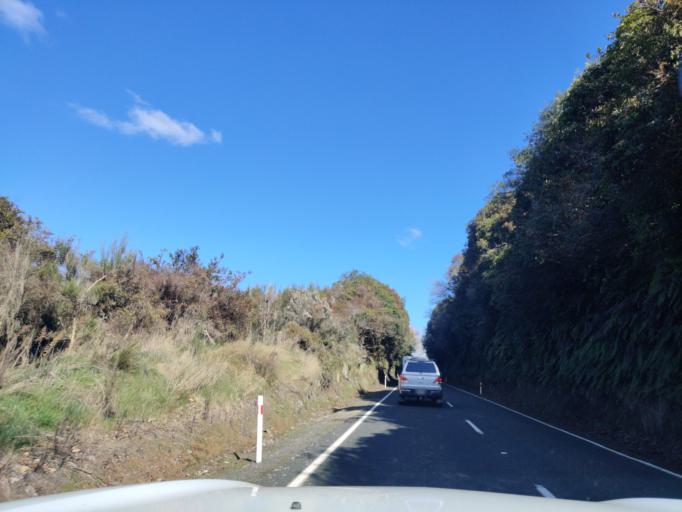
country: NZ
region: Waikato
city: Turangi
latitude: -38.7142
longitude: 175.6628
